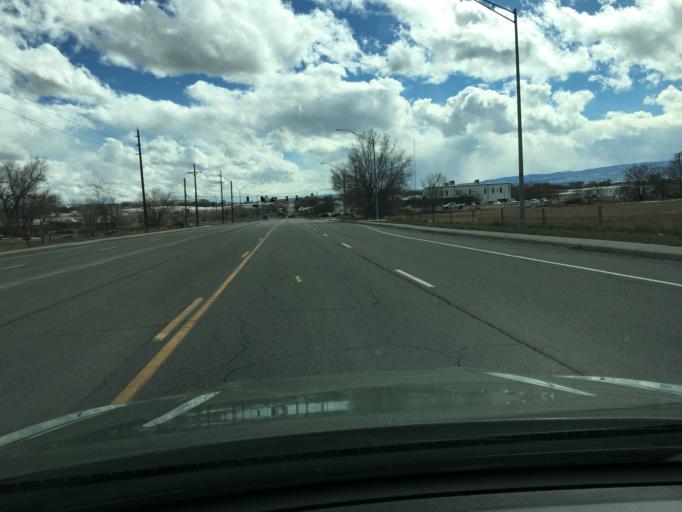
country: US
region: Colorado
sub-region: Mesa County
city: Clifton
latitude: 39.0643
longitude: -108.4595
